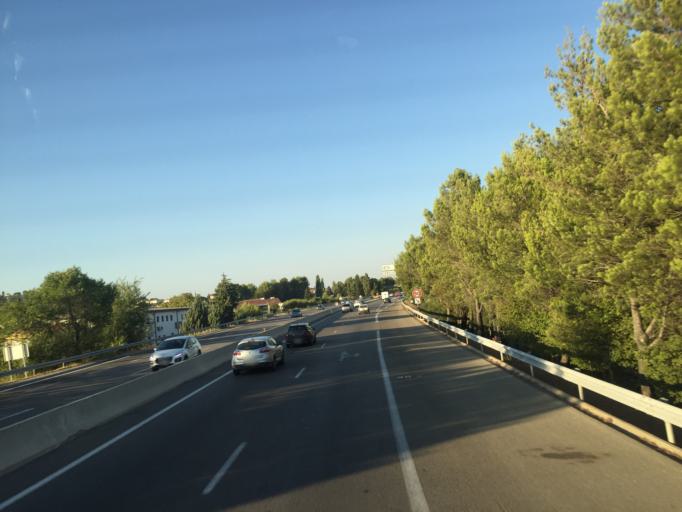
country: FR
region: Provence-Alpes-Cote d'Azur
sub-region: Departement des Bouches-du-Rhone
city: Venelles
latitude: 43.5898
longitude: 5.4800
